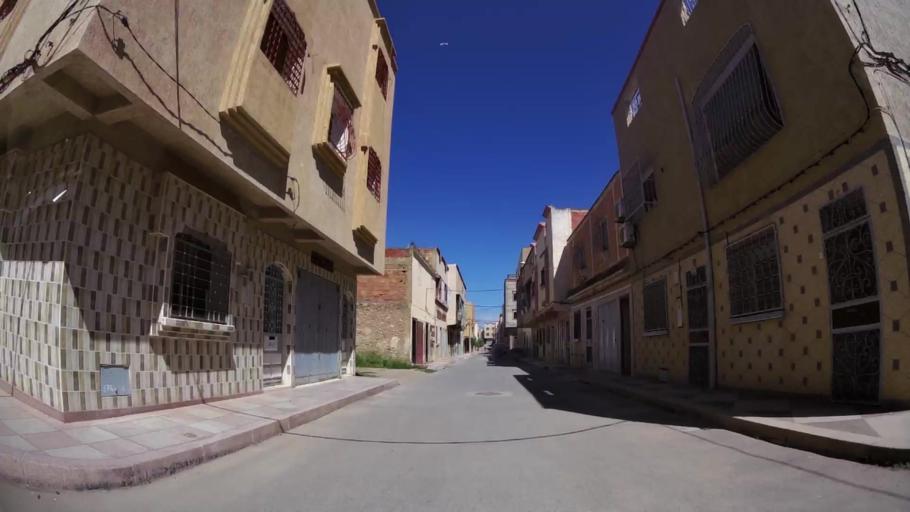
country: MA
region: Oriental
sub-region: Oujda-Angad
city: Oujda
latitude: 34.6844
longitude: -1.9373
